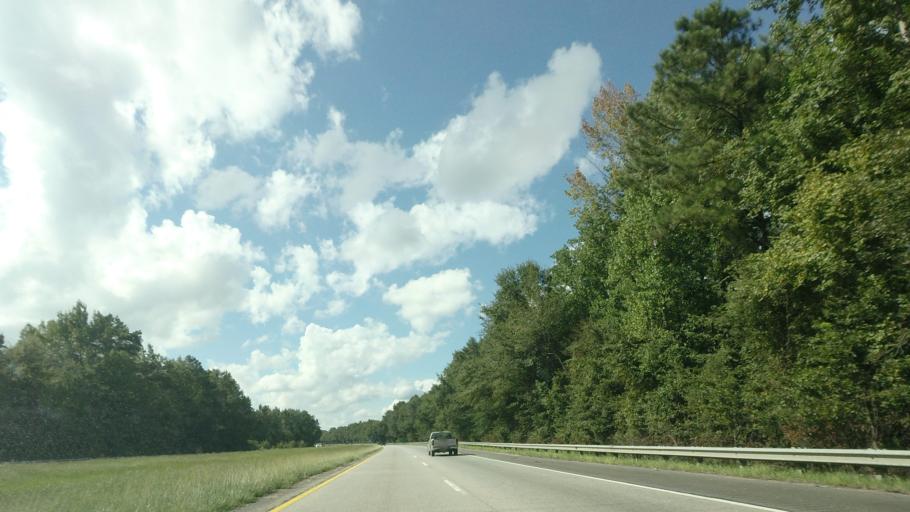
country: US
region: Georgia
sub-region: Bibb County
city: Macon
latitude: 32.8104
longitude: -83.5767
